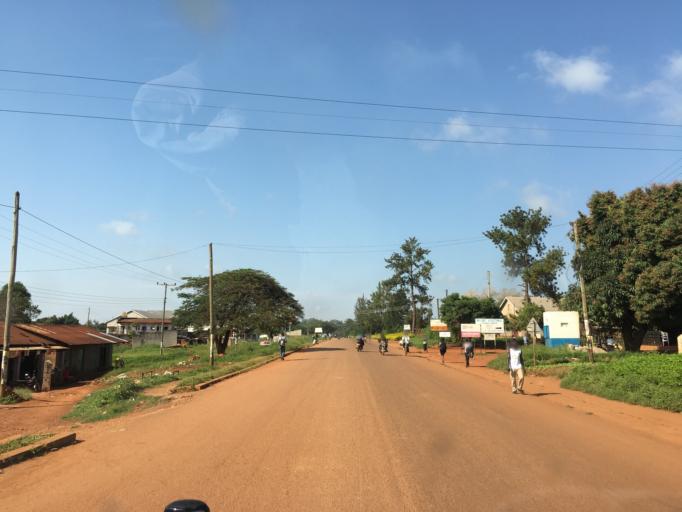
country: UG
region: Western Region
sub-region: Masindi District
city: Masindi
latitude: 1.6921
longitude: 31.7085
